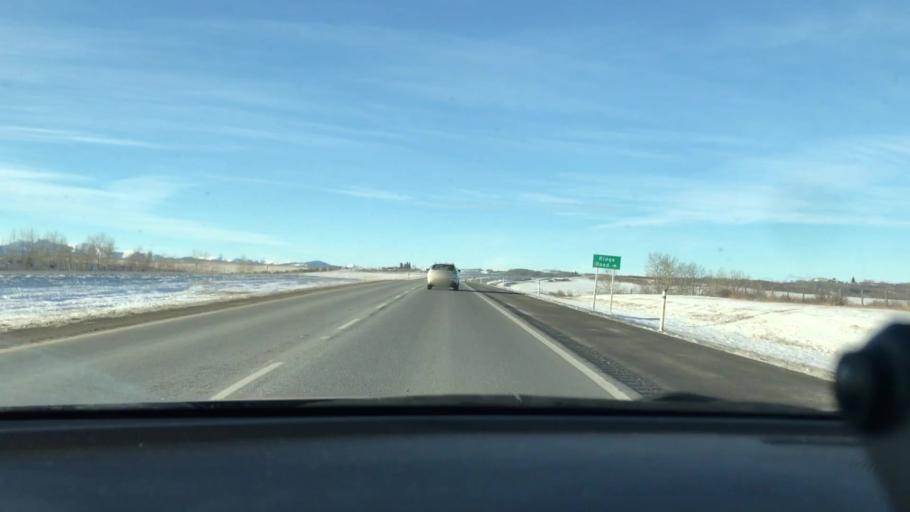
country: CA
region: Alberta
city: Cochrane
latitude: 51.0947
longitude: -114.5510
